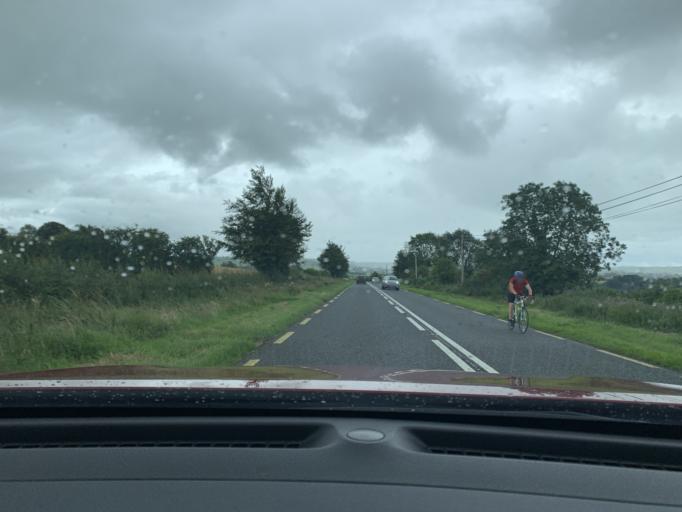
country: IE
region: Ulster
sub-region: County Donegal
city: Raphoe
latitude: 54.7967
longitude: -7.5638
